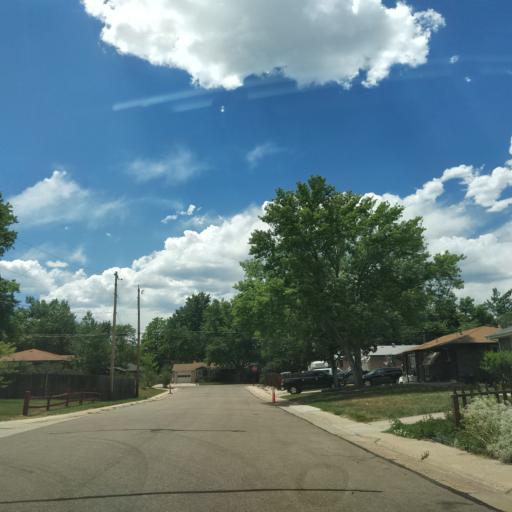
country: US
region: Colorado
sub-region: Jefferson County
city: Lakewood
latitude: 39.6887
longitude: -105.0879
